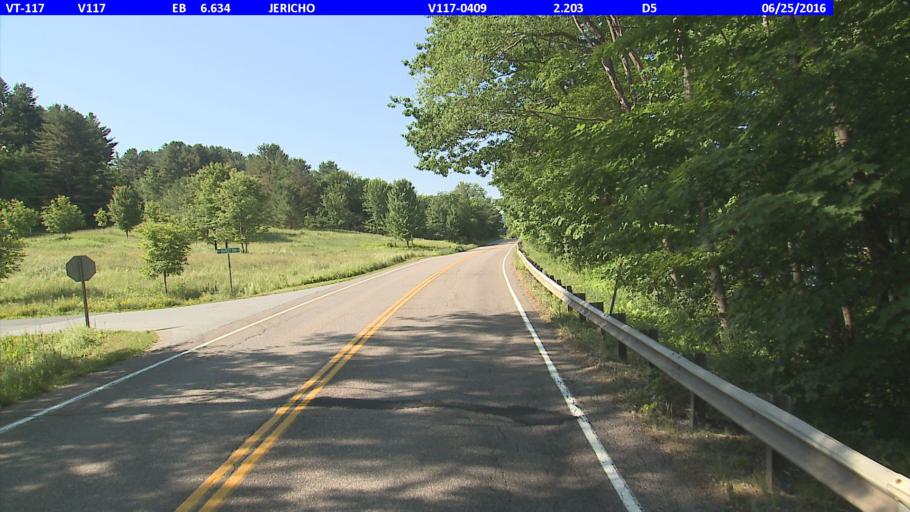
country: US
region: Vermont
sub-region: Chittenden County
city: Williston
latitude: 44.4439
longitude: -73.0190
